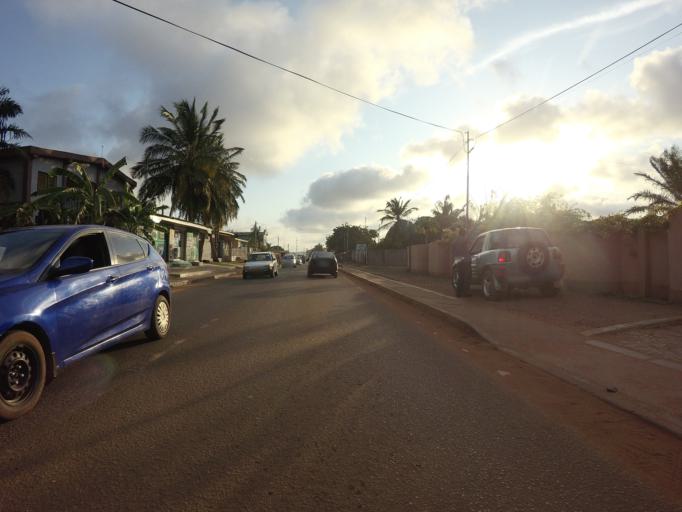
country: GH
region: Greater Accra
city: Teshi Old Town
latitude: 5.5961
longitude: -0.1201
